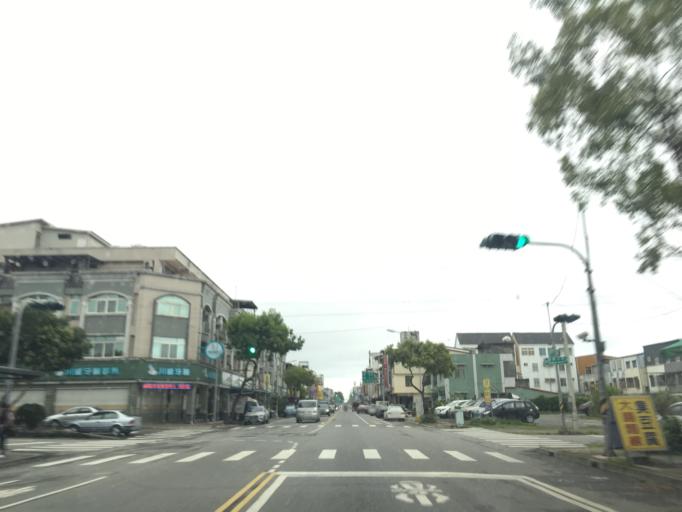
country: TW
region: Taiwan
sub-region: Hualien
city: Hualian
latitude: 23.9776
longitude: 121.5660
